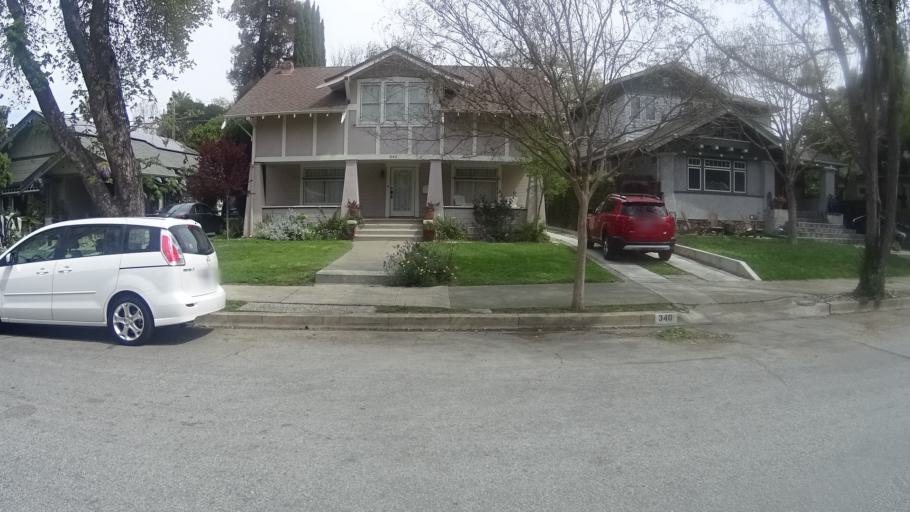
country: US
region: California
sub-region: Santa Clara County
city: San Jose
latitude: 37.3382
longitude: -121.8714
